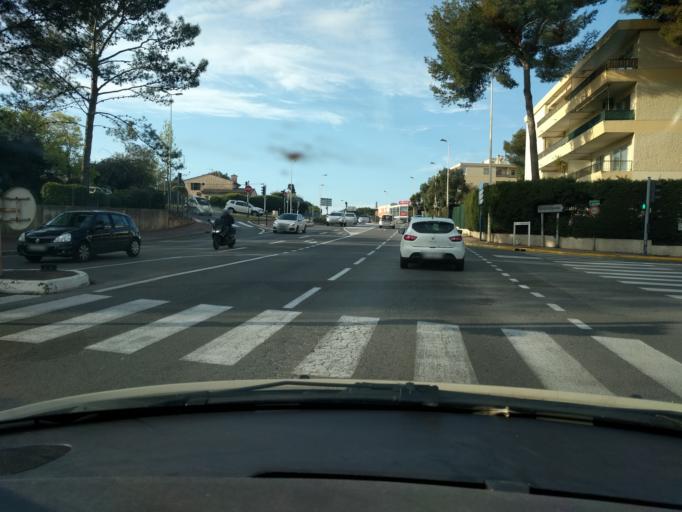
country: FR
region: Provence-Alpes-Cote d'Azur
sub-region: Departement des Alpes-Maritimes
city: Cannes
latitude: 43.5694
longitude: 6.9816
